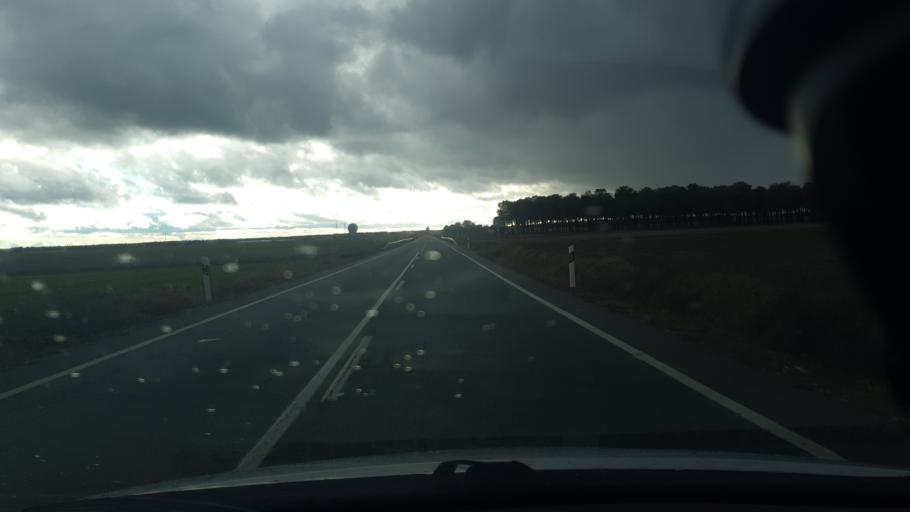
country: ES
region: Castille and Leon
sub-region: Provincia de Segovia
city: Chane
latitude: 41.3126
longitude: -4.3930
